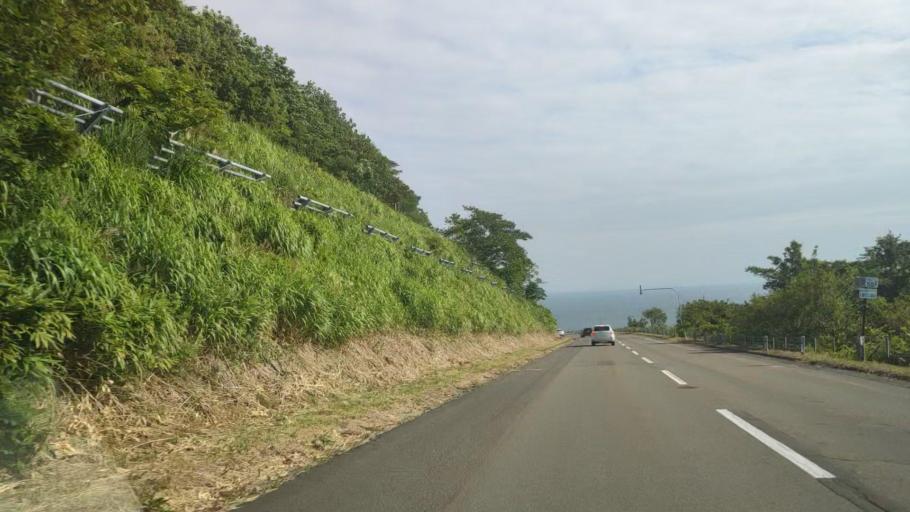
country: JP
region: Hokkaido
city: Ishikari
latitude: 43.4961
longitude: 141.3743
